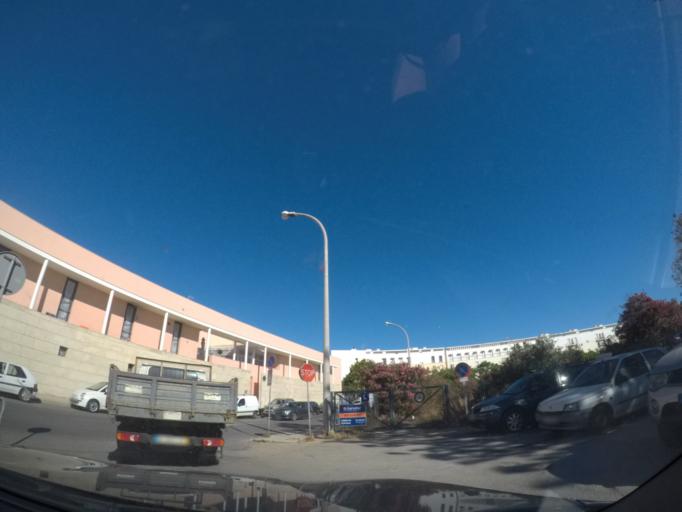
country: PT
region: Faro
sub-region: Lagos
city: Lagos
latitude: 37.1094
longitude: -8.6730
